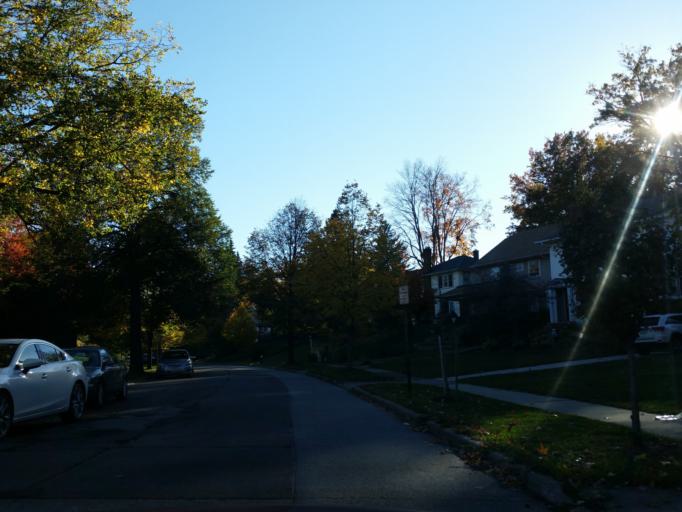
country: US
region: Ohio
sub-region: Cuyahoga County
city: Lakewood
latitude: 41.4841
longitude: -81.7839
